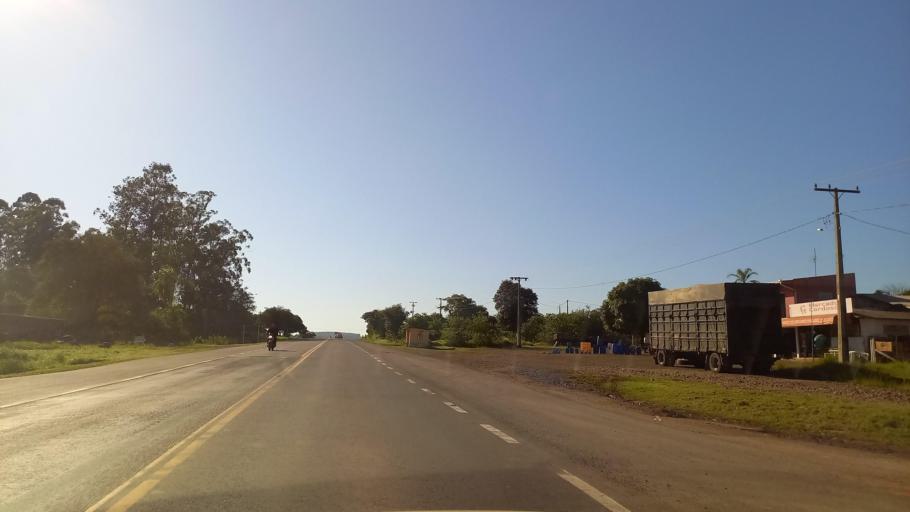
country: BR
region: Rio Grande do Sul
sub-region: Taquari
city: Taquari
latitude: -29.7028
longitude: -51.8573
